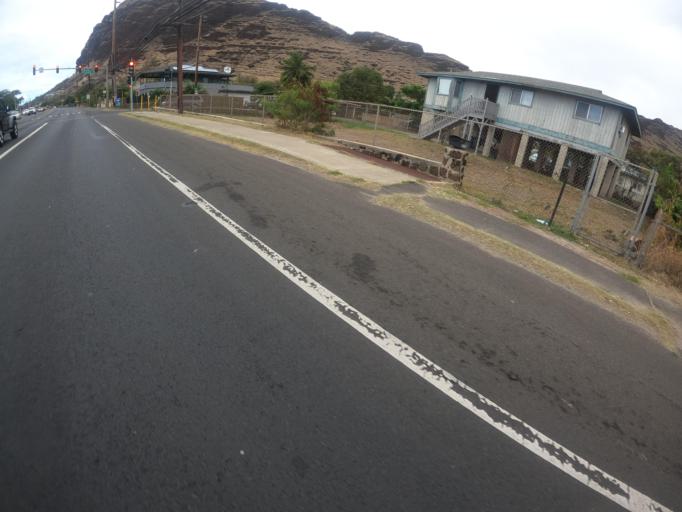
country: US
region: Hawaii
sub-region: Honolulu County
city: Nanakuli
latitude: 21.3966
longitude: -158.1630
